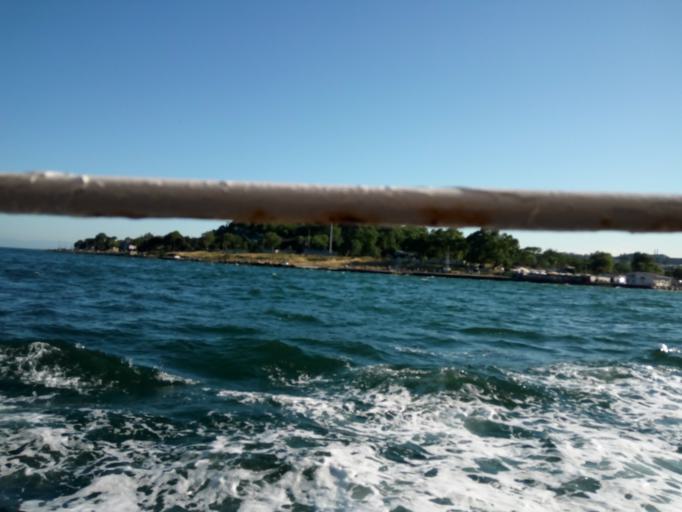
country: TR
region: Istanbul
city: Eminoenue
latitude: 41.0191
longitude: 28.9879
